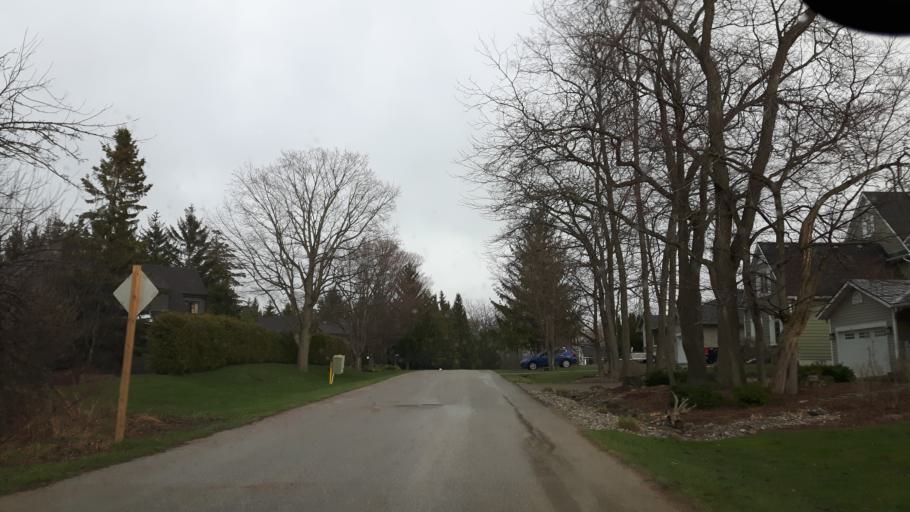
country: CA
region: Ontario
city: Bluewater
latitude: 43.5712
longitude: -81.7050
